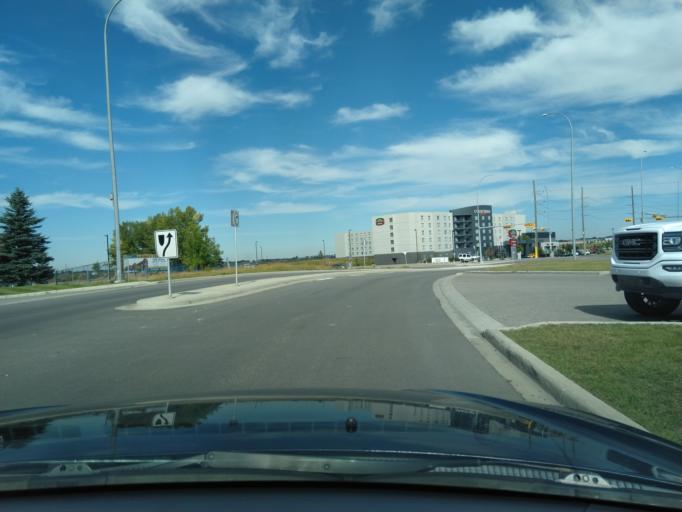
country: CA
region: Alberta
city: Calgary
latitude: 51.0957
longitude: -114.0032
